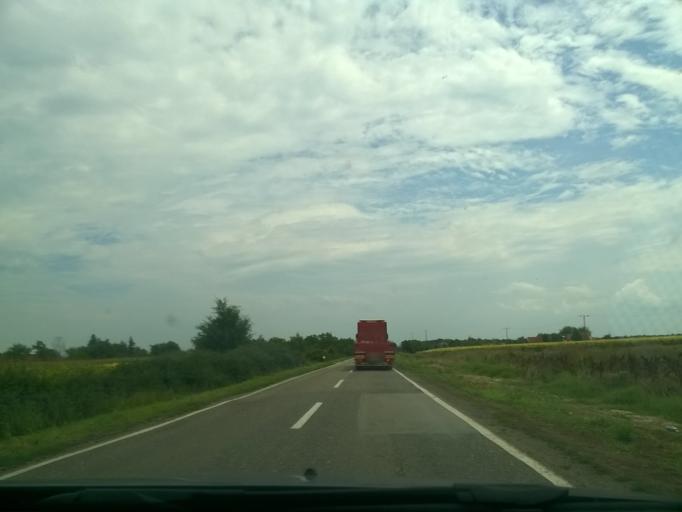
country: RS
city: Klek
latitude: 45.3867
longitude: 20.4861
